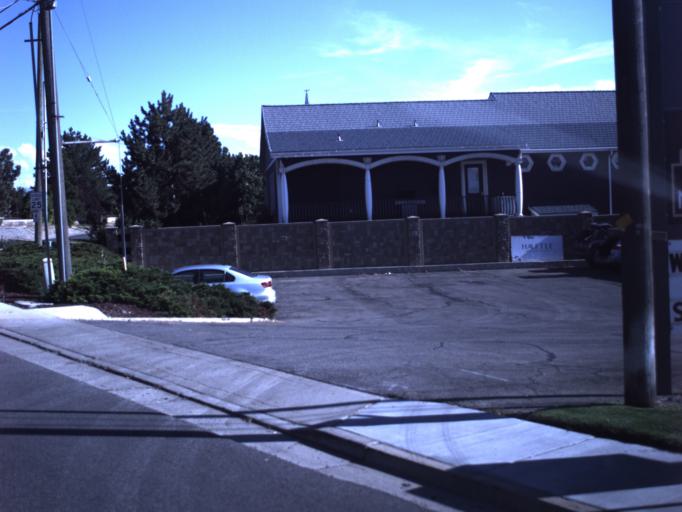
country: US
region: Utah
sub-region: Utah County
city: Lindon
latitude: 40.3361
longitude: -111.7156
